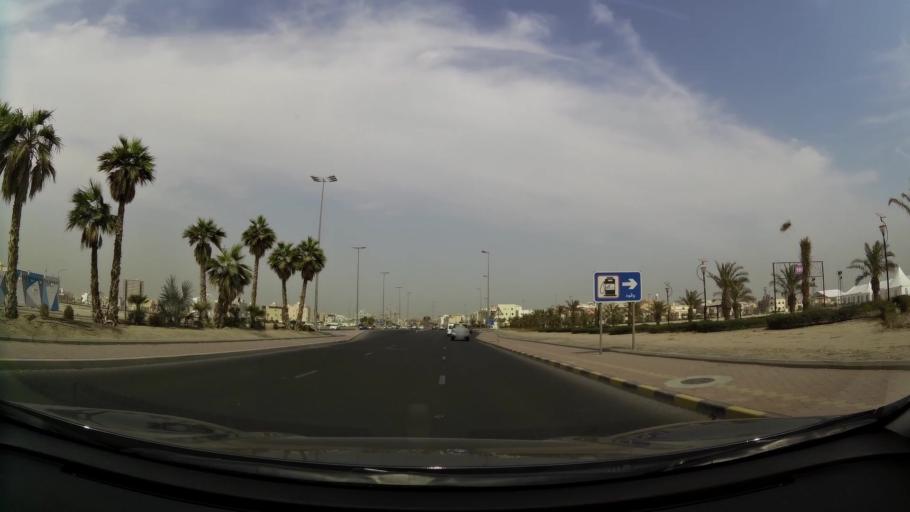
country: KW
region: Al Farwaniyah
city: Janub as Surrah
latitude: 29.2881
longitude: 48.0027
